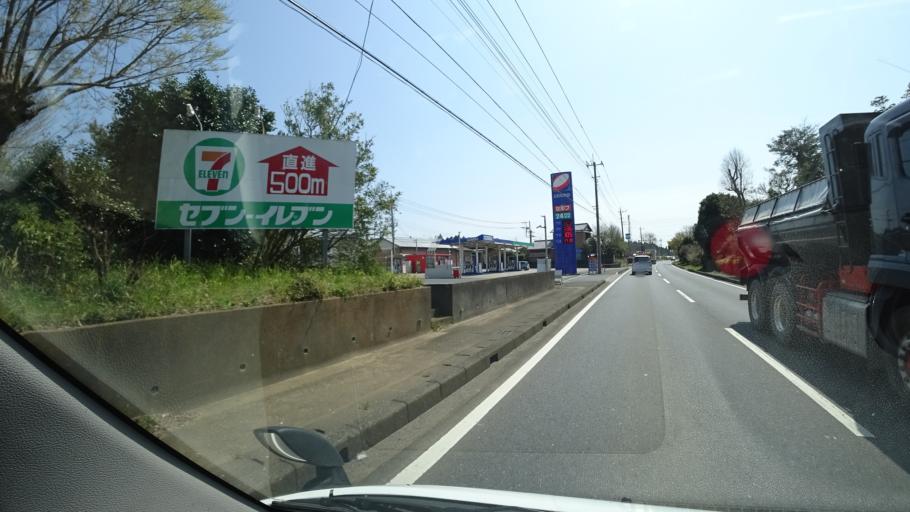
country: JP
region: Chiba
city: Naruto
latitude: 35.6686
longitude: 140.4372
